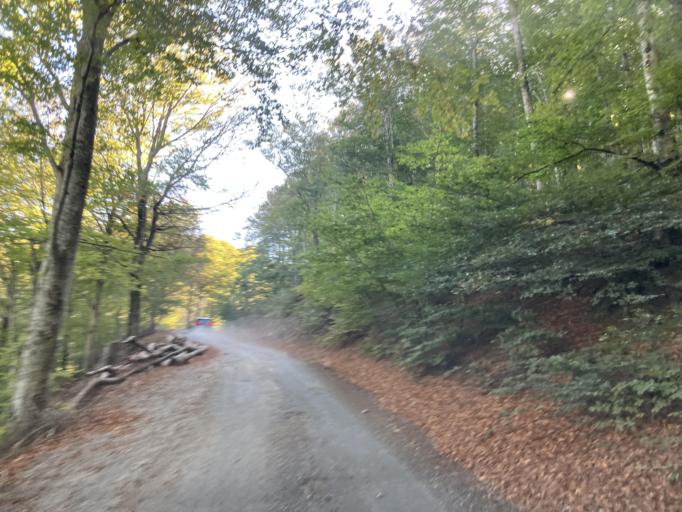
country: FR
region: Languedoc-Roussillon
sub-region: Departement des Pyrenees-Orientales
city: la Roca d'Albera
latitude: 42.4783
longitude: 2.9297
